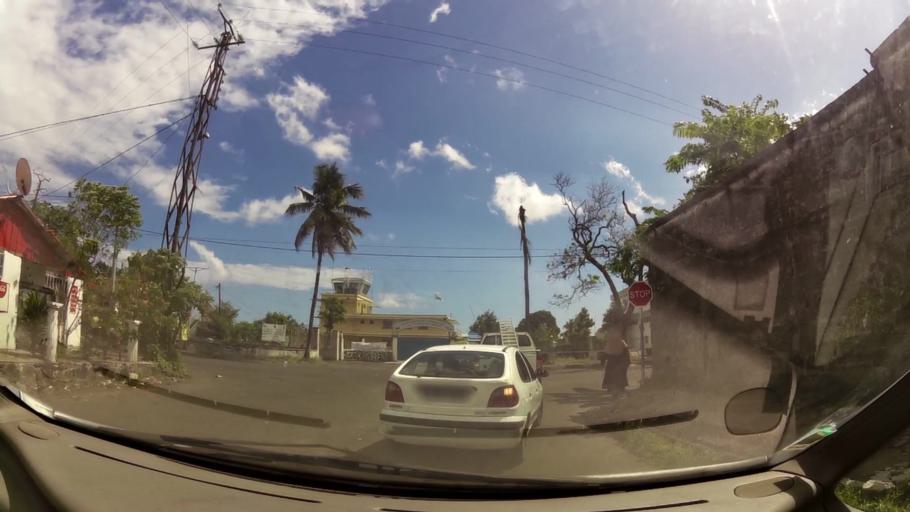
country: KM
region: Grande Comore
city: Mavingouni
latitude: -11.7087
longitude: 43.2473
